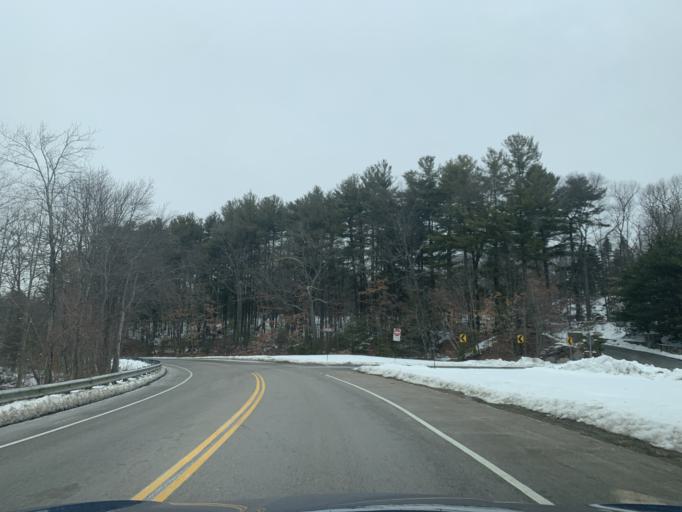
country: US
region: Massachusetts
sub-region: Norfolk County
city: Milton
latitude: 42.2361
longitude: -71.0901
